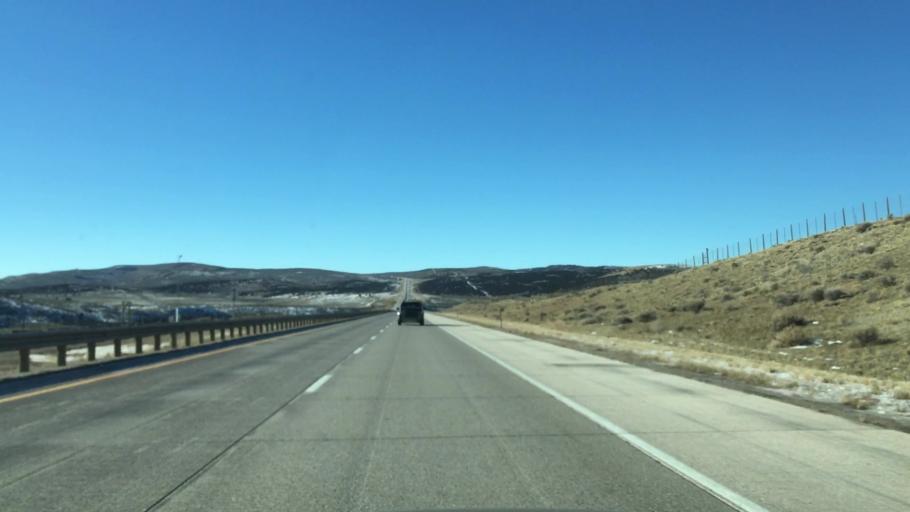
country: US
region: Wyoming
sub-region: Uinta County
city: Mountain View
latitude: 41.2983
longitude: -110.6143
